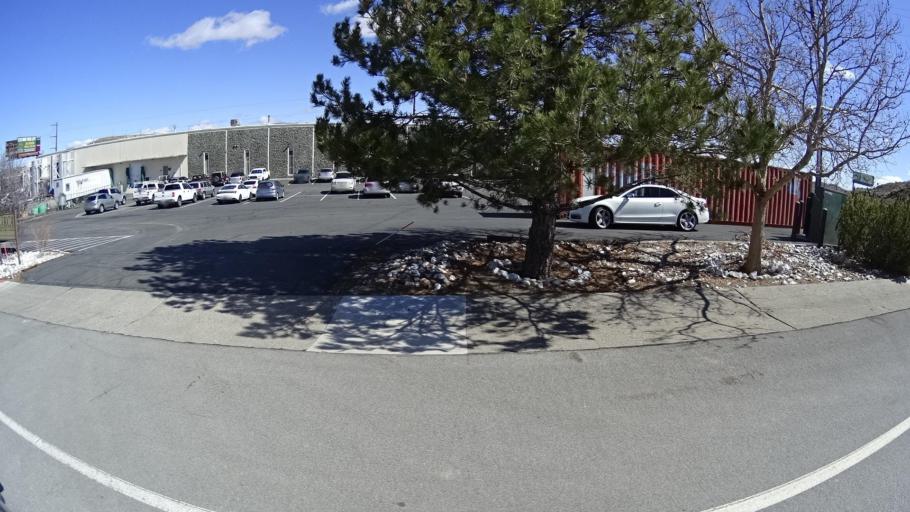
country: US
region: Nevada
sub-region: Washoe County
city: Golden Valley
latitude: 39.5939
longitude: -119.8333
